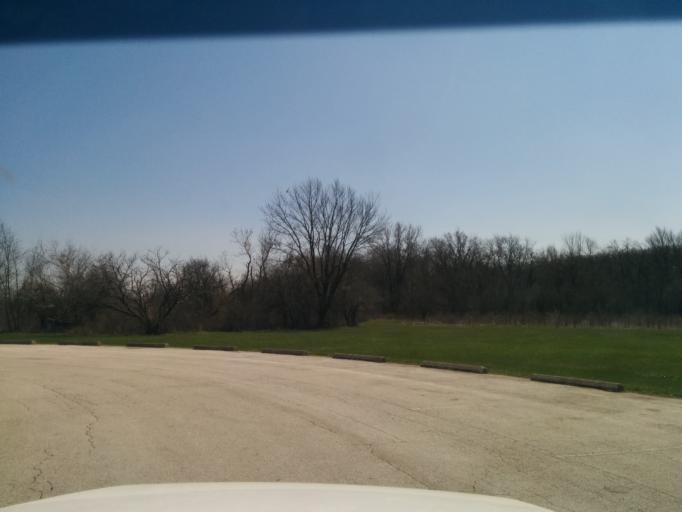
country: US
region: Illinois
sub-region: Cook County
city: Midlothian
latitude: 41.6104
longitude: -87.7263
